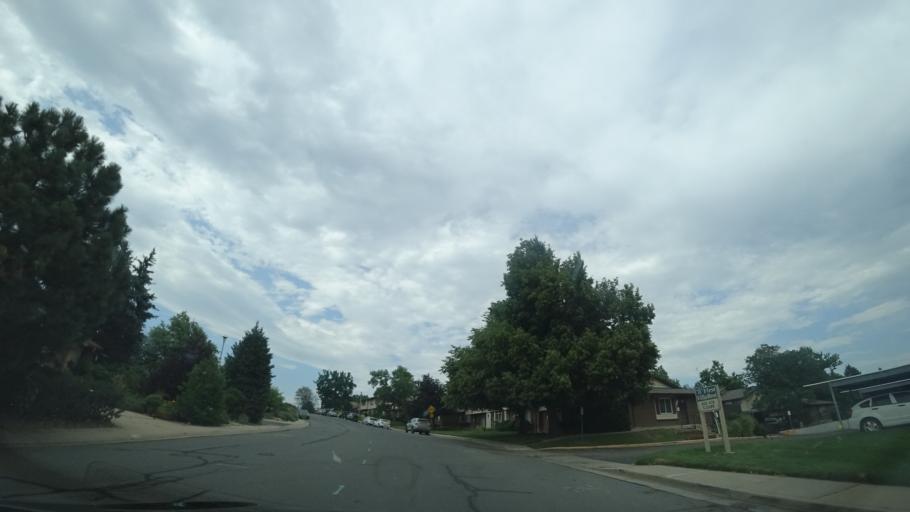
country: US
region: Colorado
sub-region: Jefferson County
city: Lakewood
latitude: 39.7080
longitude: -105.0912
